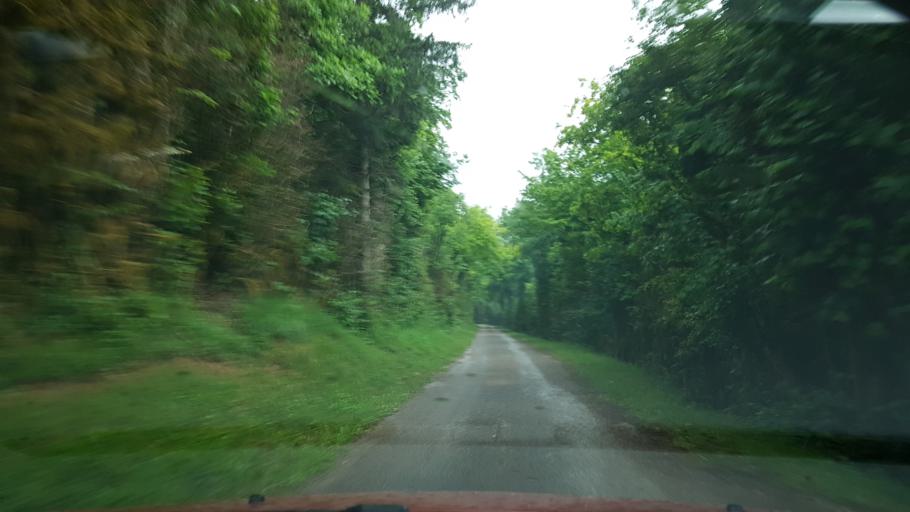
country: FR
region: Franche-Comte
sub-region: Departement du Jura
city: Clairvaux-les-Lacs
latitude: 46.5292
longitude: 5.7145
